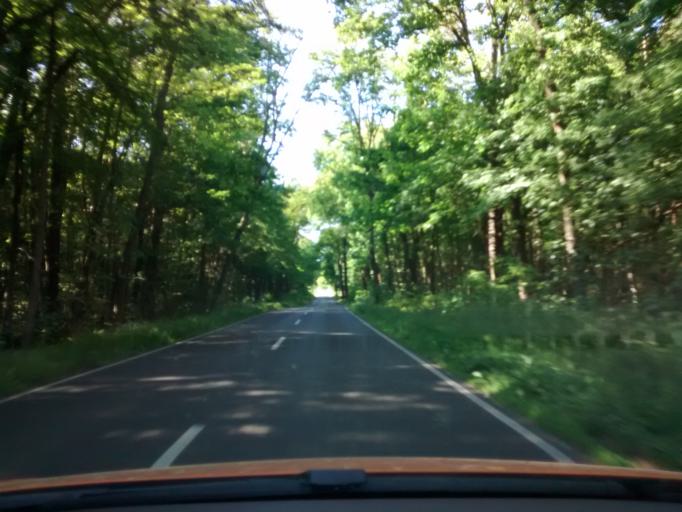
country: DE
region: Brandenburg
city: Bad Saarow
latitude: 52.2627
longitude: 14.0731
